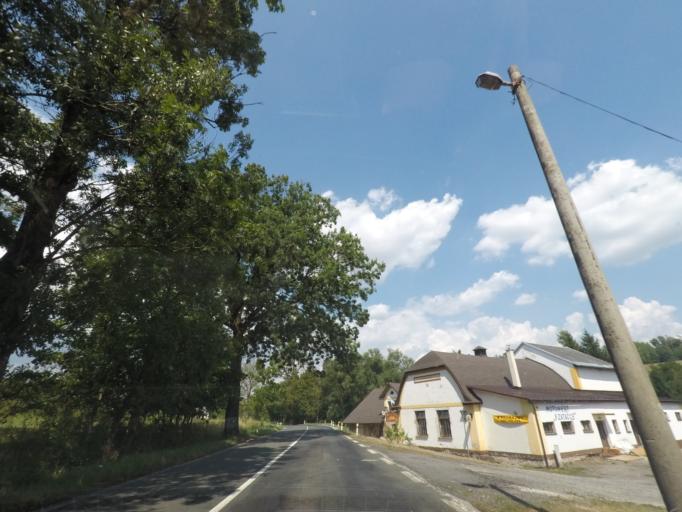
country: CZ
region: Kralovehradecky
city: Zadni Mostek
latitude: 50.5323
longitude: 15.6773
